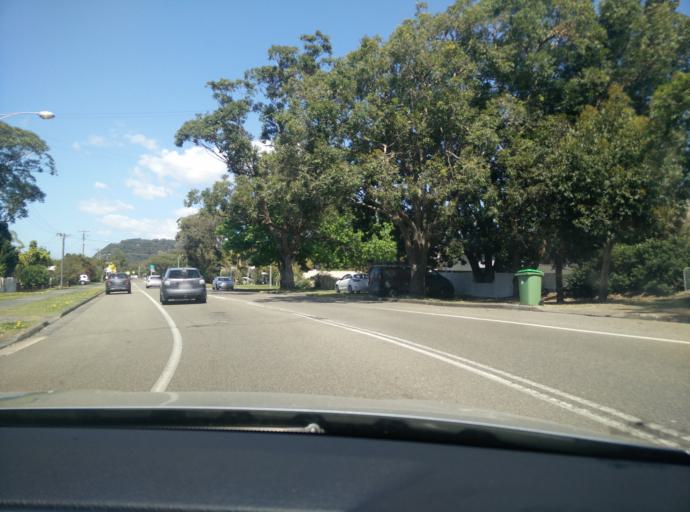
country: AU
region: New South Wales
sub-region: Gosford Shire
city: Umina
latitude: -33.5219
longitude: 151.3153
